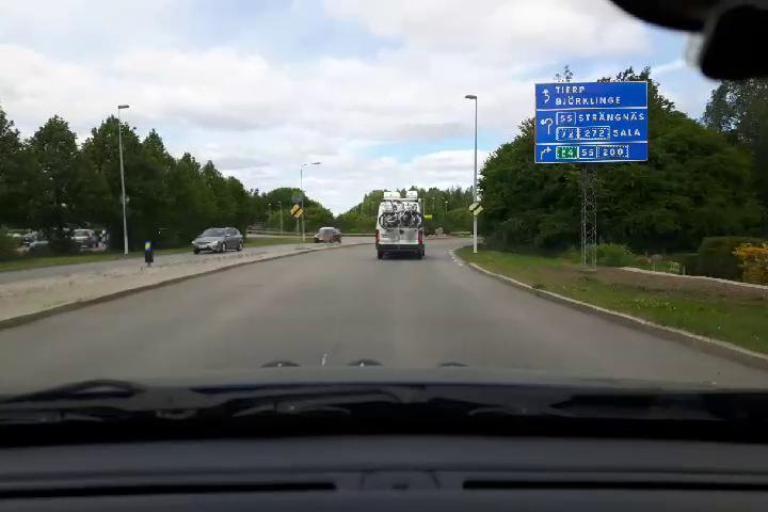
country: SE
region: Uppsala
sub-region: Uppsala Kommun
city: Gamla Uppsala
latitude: 59.8793
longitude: 17.6225
